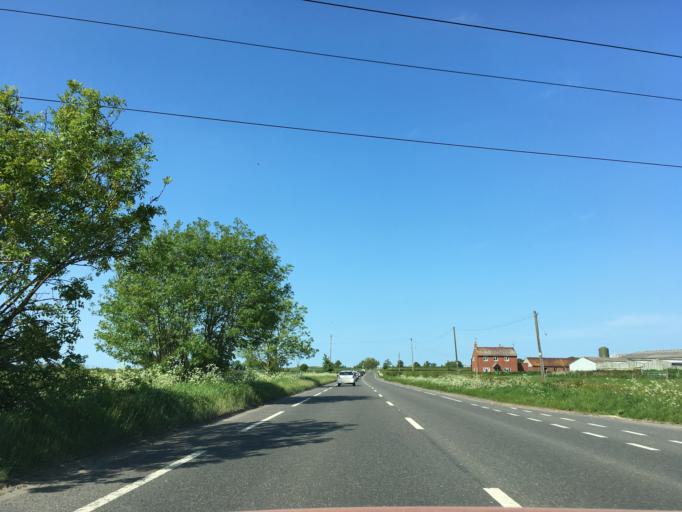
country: GB
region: England
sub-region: Gloucestershire
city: Dursley
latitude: 51.7428
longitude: -2.3530
